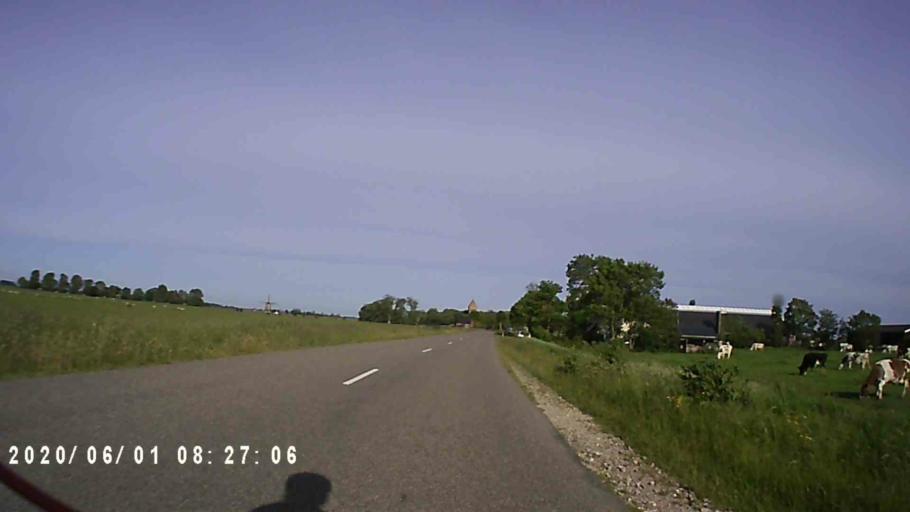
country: NL
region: Friesland
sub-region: Gemeente Ferwerderadiel
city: Burdaard
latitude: 53.2999
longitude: 5.8580
